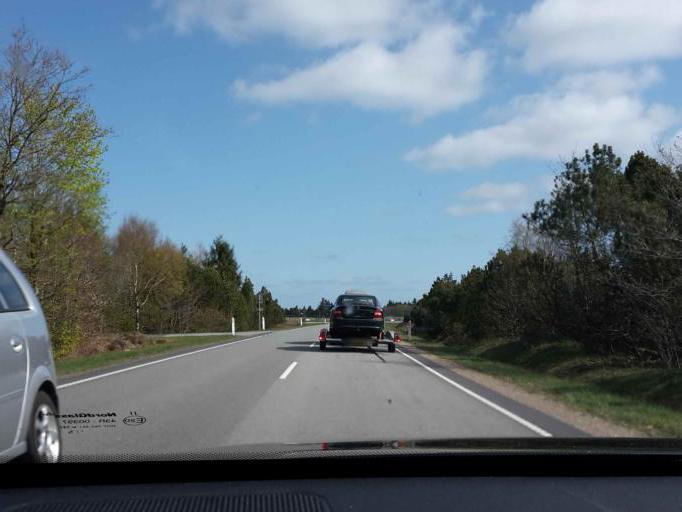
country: DK
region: South Denmark
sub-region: Billund Kommune
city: Grindsted
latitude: 55.6757
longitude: 8.9582
